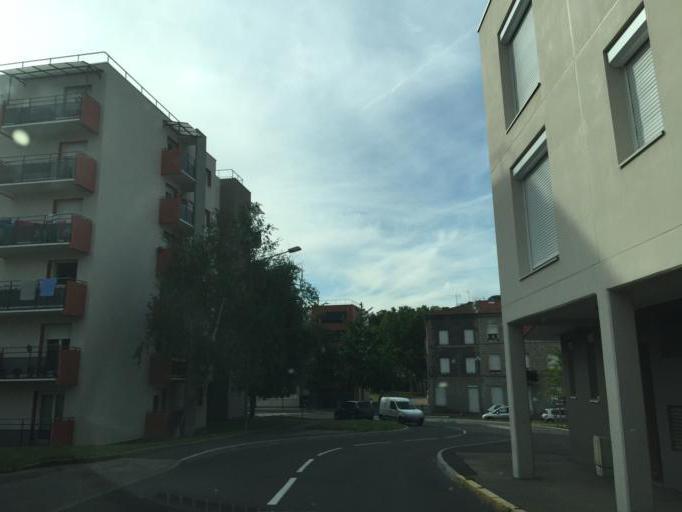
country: FR
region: Rhone-Alpes
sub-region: Departement de la Loire
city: Saint-Chamond
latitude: 45.4805
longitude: 4.5273
